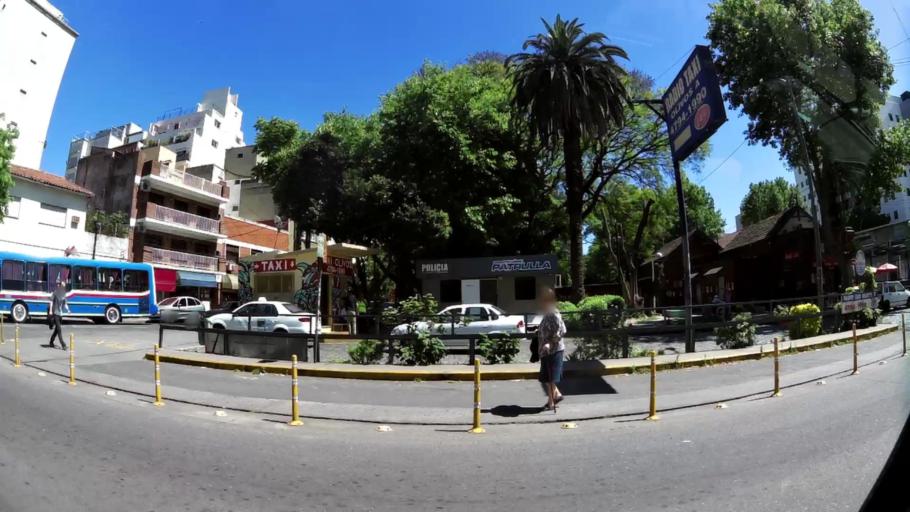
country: AR
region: Buenos Aires
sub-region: Partido de Vicente Lopez
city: Olivos
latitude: -34.5087
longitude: -58.4805
